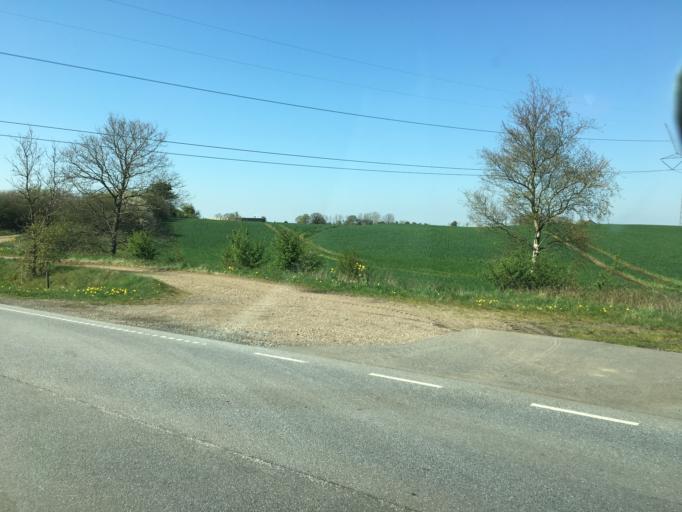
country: DK
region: South Denmark
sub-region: Haderslev Kommune
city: Vojens
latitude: 55.2951
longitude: 9.3856
